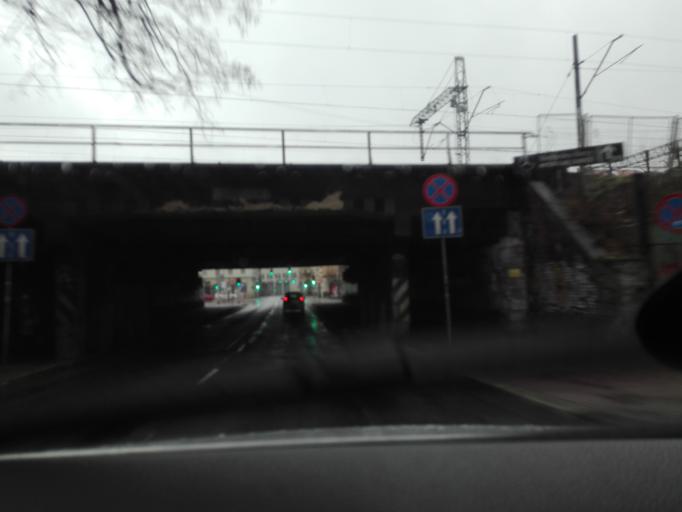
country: PL
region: Silesian Voivodeship
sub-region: Katowice
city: Katowice
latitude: 50.2561
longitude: 19.0279
